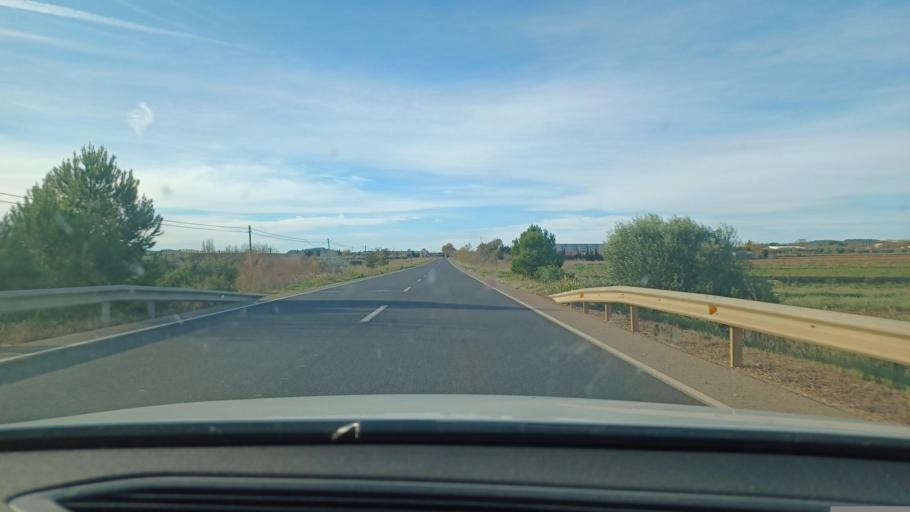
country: ES
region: Catalonia
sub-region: Provincia de Tarragona
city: Ulldecona
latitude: 40.6117
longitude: 0.4633
